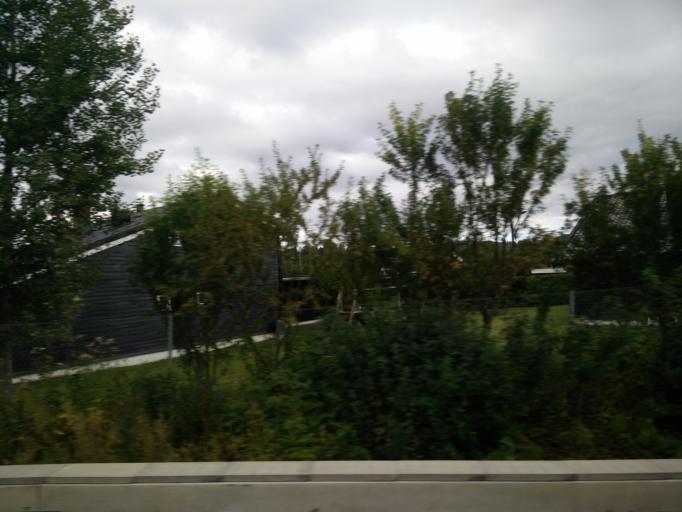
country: NO
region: Akershus
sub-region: Baerum
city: Lysaker
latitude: 59.9499
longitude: 10.6308
